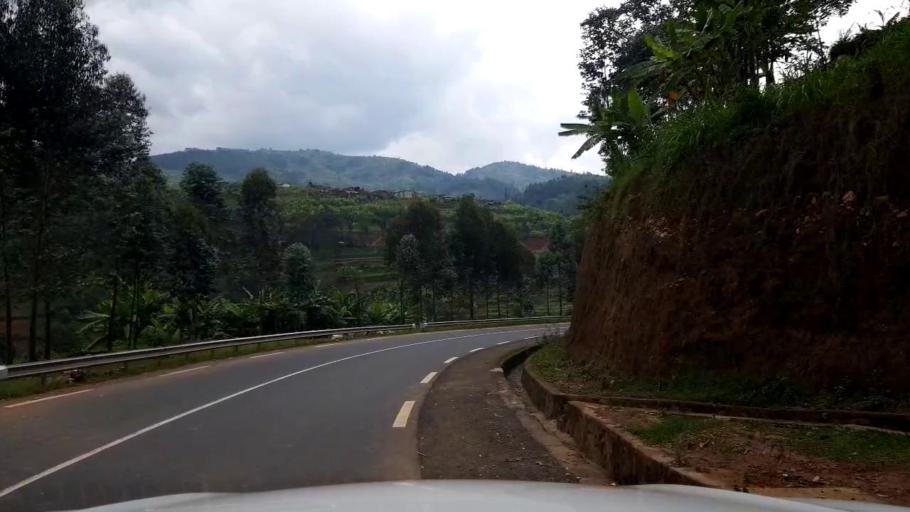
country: RW
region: Western Province
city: Kibuye
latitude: -1.9103
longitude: 29.3687
